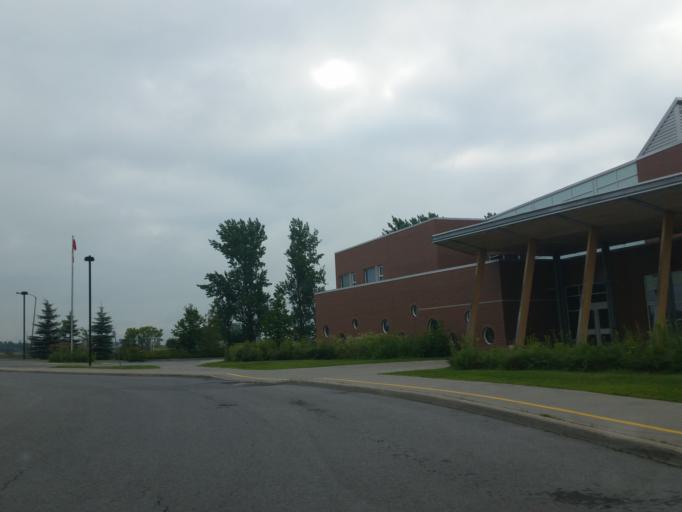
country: CA
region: Ontario
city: Clarence-Rockland
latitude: 45.4219
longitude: -75.4172
